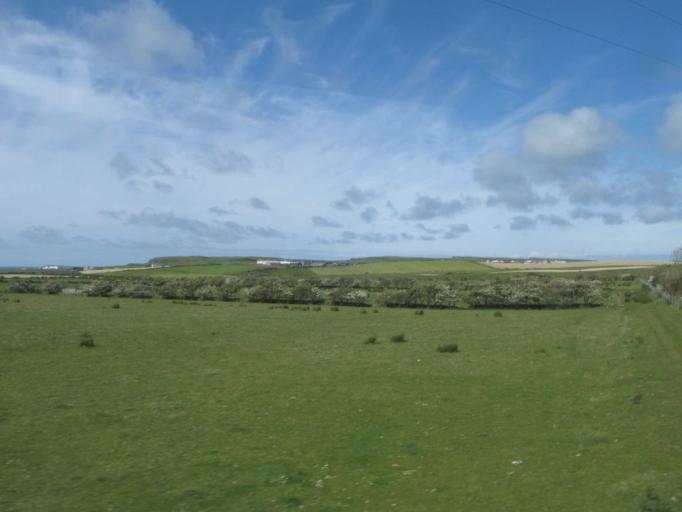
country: GB
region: Northern Ireland
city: Bushmills
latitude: 55.2206
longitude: -6.5095
